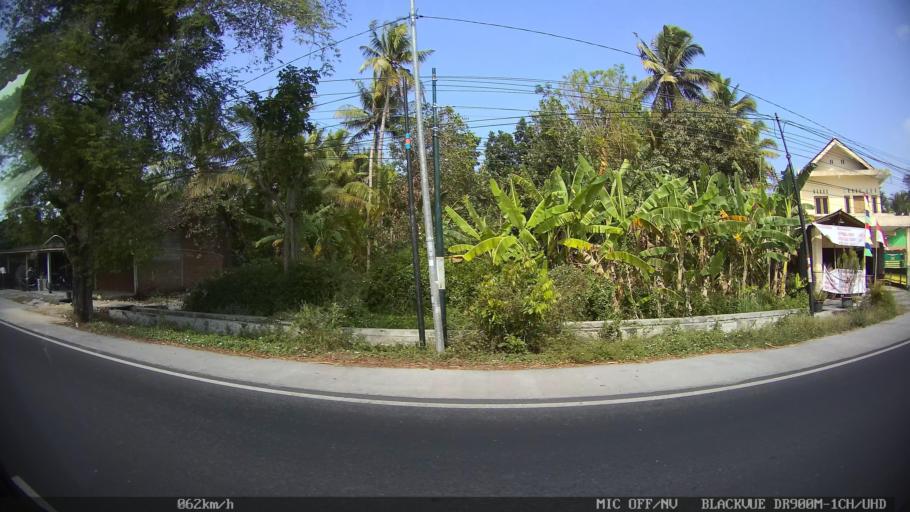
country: ID
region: Daerah Istimewa Yogyakarta
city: Srandakan
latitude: -7.9038
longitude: 110.1688
